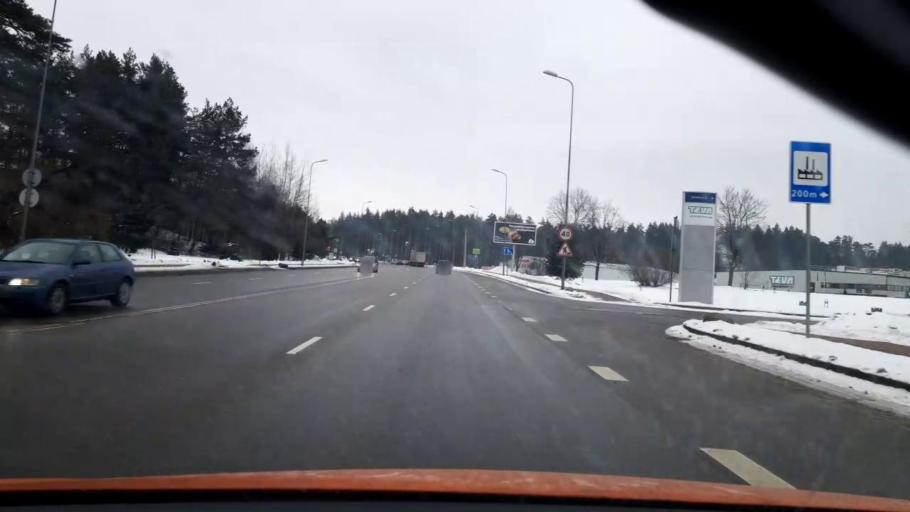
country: LT
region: Vilnius County
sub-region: Vilnius
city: Fabijoniskes
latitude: 54.7551
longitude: 25.2710
